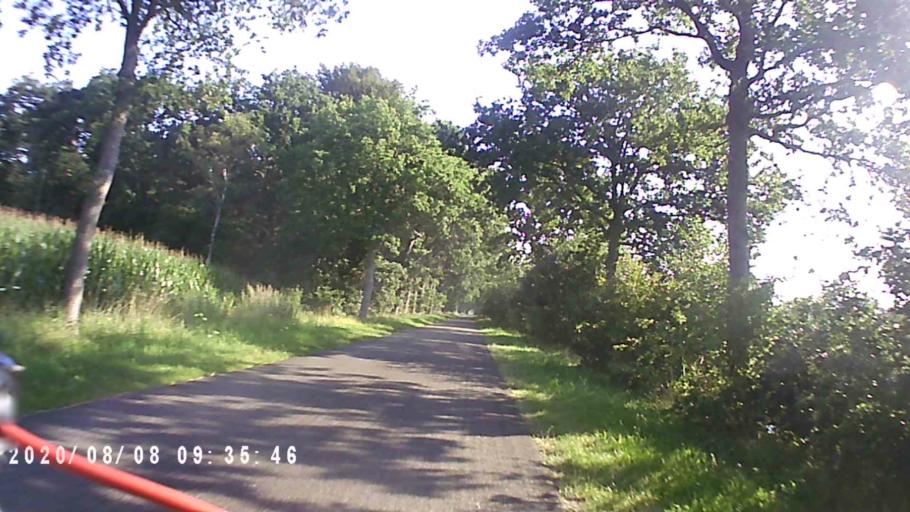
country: NL
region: Groningen
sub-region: Gemeente Leek
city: Leek
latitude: 53.0477
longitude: 6.3832
